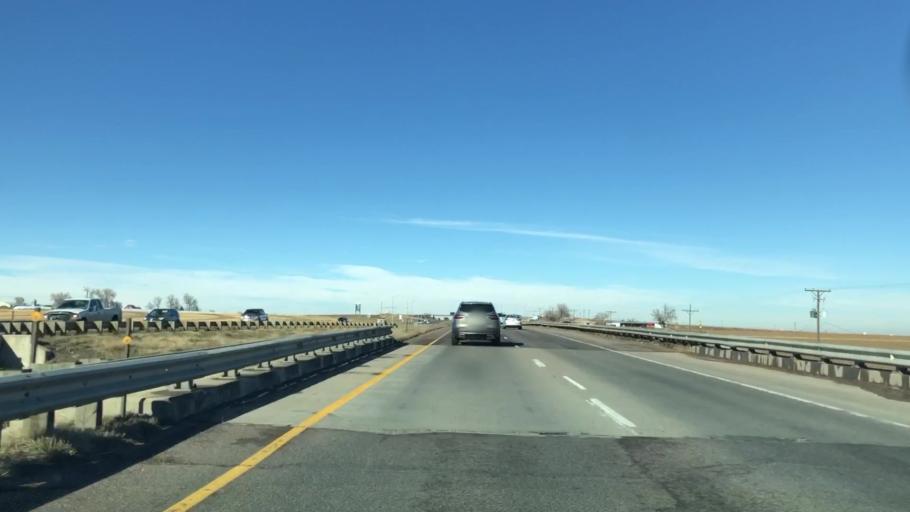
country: US
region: Colorado
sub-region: Weld County
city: Johnstown
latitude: 40.3282
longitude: -104.9801
